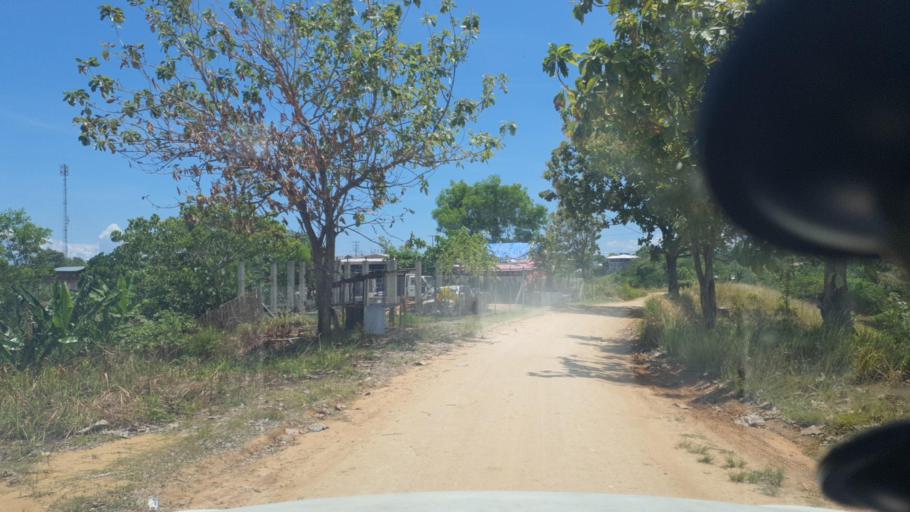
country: SB
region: Guadalcanal
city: Honiara
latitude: -9.4362
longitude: 159.9275
